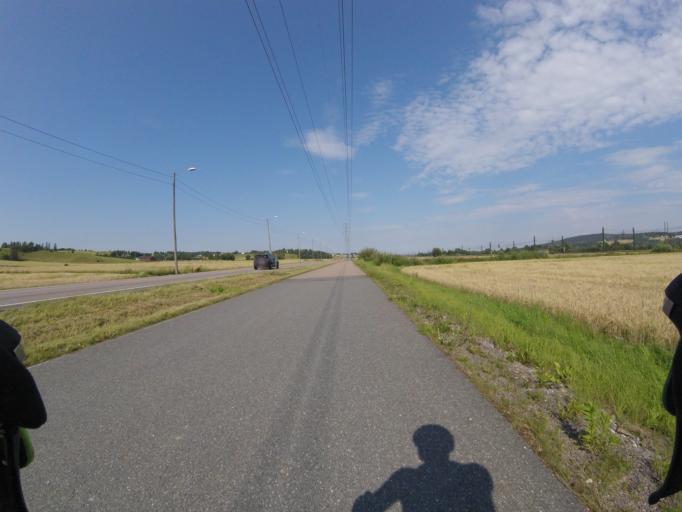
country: NO
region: Akershus
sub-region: Skedsmo
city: Lillestrom
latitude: 59.9751
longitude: 11.0682
